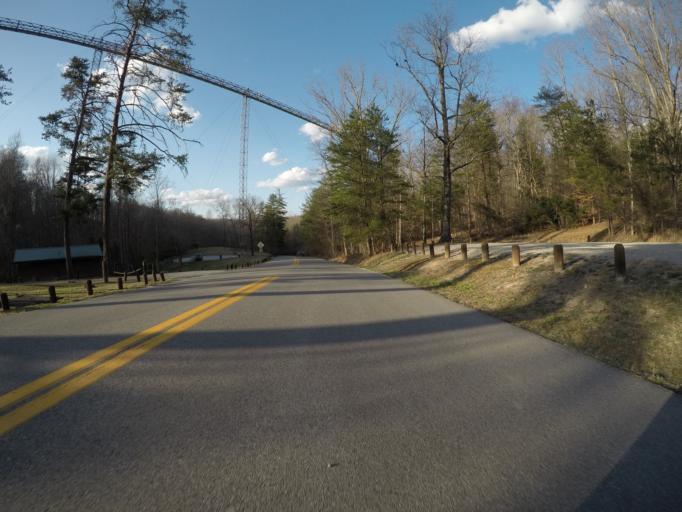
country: US
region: West Virginia
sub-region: Kanawha County
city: Charleston
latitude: 38.3843
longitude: -81.5801
